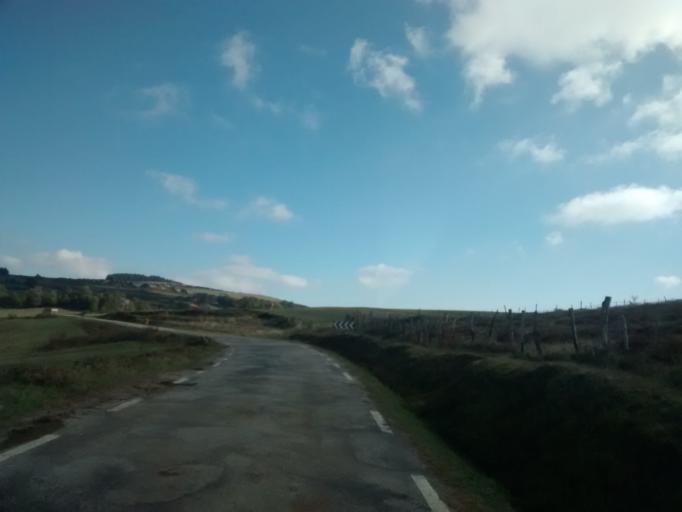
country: ES
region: Castille and Leon
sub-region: Provincia de Burgos
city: Arija
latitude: 42.9249
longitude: -4.0079
